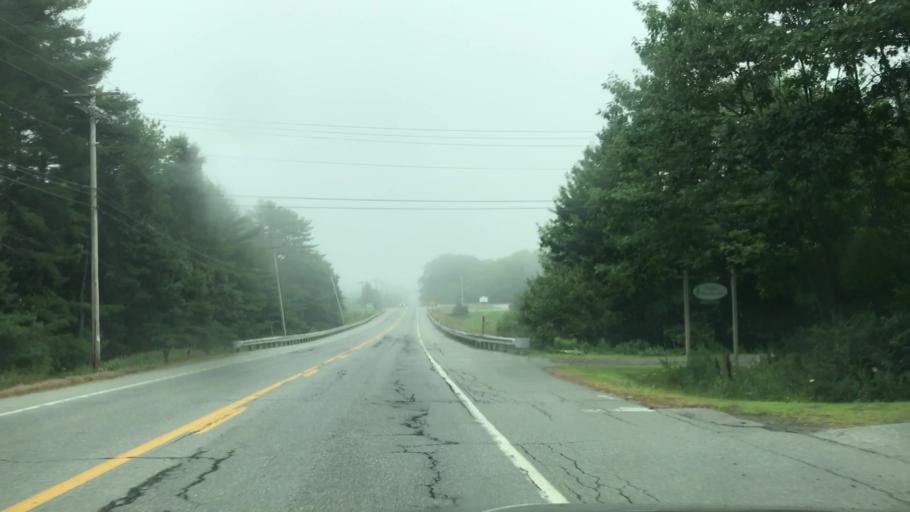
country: US
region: Maine
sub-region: Knox County
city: Warren
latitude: 44.1198
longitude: -69.2568
